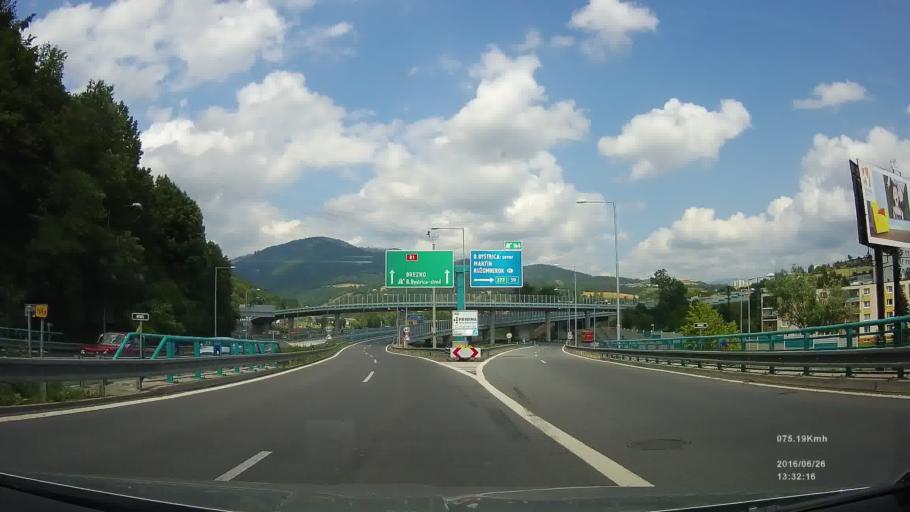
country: SK
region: Banskobystricky
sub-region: Okres Banska Bystrica
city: Banska Bystrica
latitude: 48.7477
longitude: 19.1390
